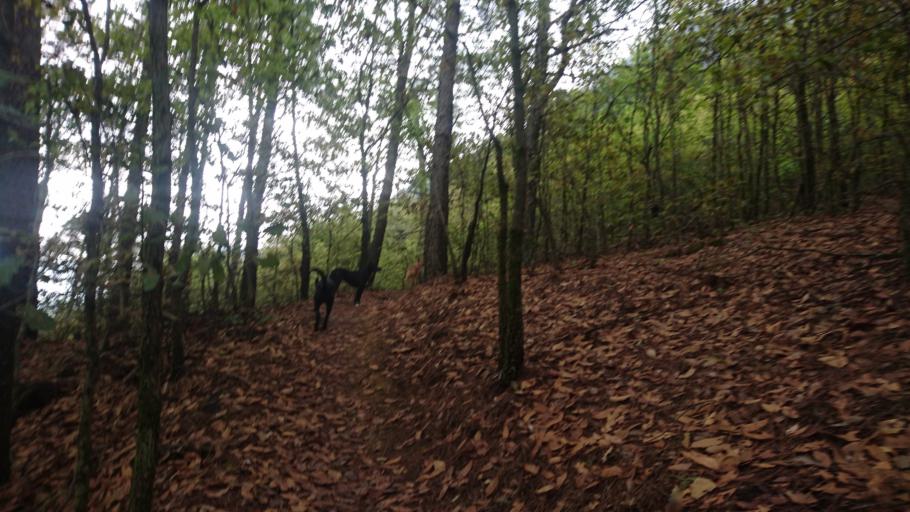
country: MX
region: Nuevo Leon
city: Garza Garcia
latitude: 25.6033
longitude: -100.3362
